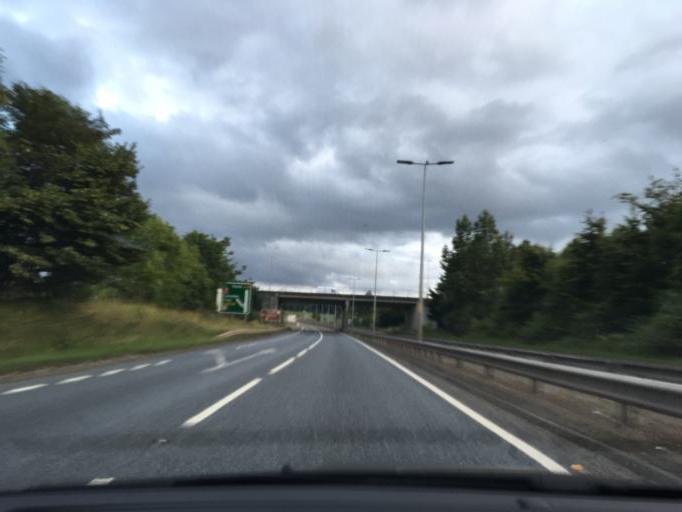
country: GB
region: Scotland
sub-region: Highland
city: Inverness
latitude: 57.4731
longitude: -4.1856
